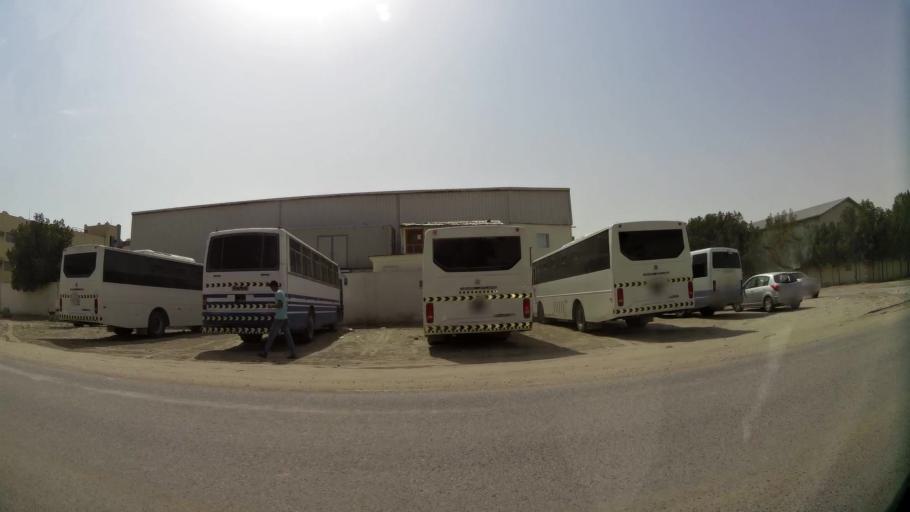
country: QA
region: Al Wakrah
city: Al Wukayr
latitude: 25.1700
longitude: 51.4647
